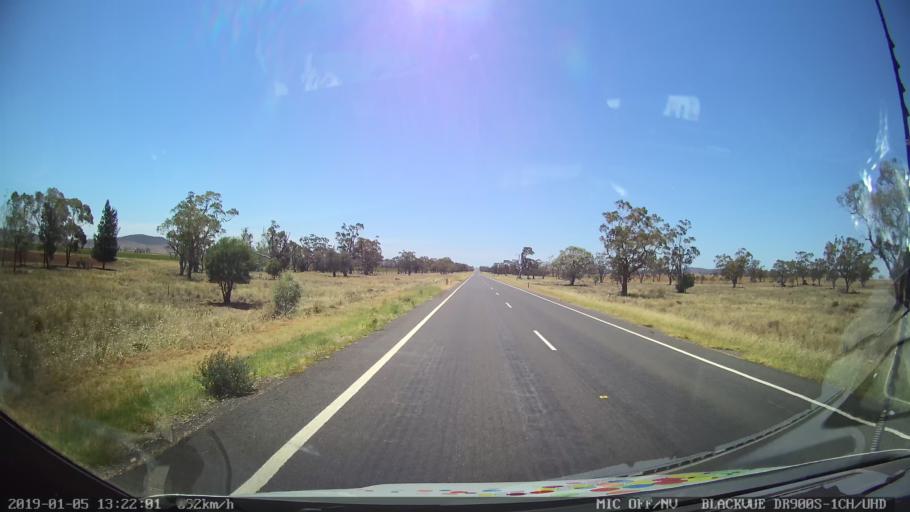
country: AU
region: New South Wales
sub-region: Gunnedah
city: Gunnedah
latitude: -31.0896
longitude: 149.9563
